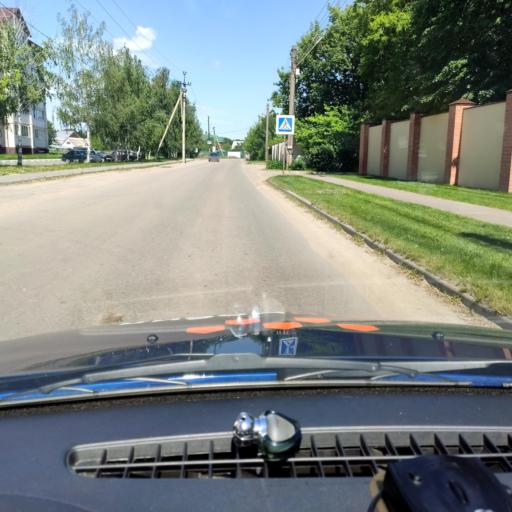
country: RU
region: Voronezj
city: Ramon'
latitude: 51.8270
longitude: 39.2659
